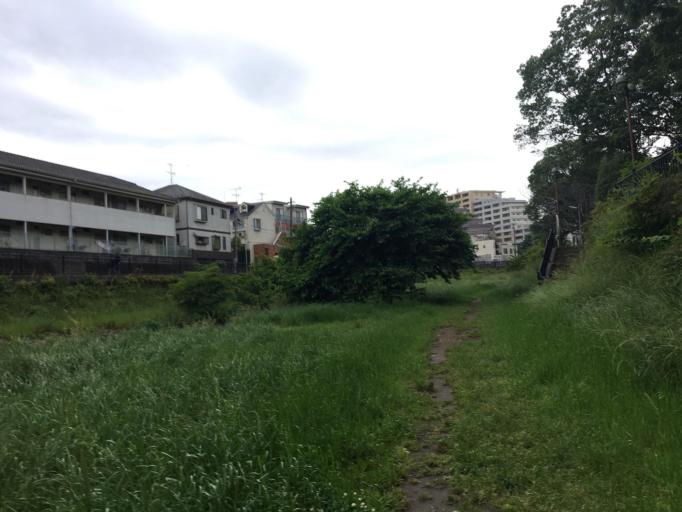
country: JP
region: Tokyo
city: Chofugaoka
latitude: 35.6490
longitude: 139.5700
